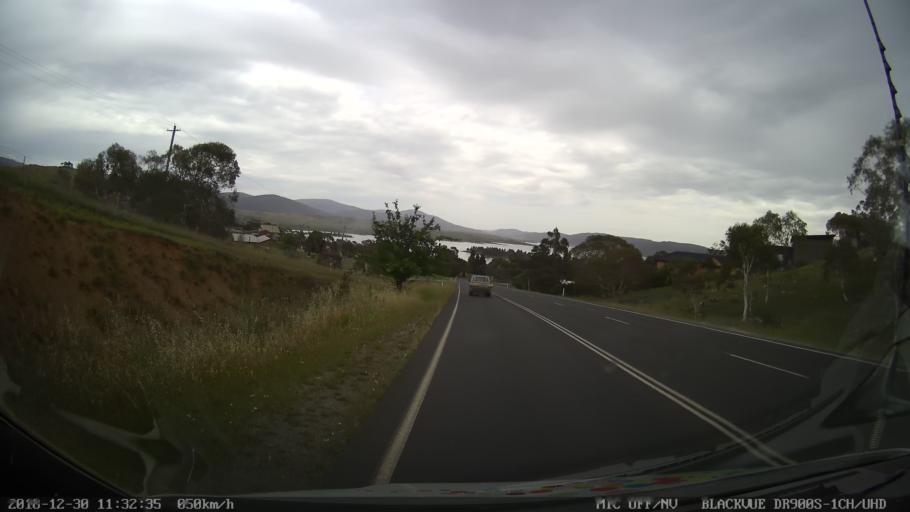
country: AU
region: New South Wales
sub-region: Snowy River
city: Jindabyne
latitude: -36.4209
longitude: 148.6103
